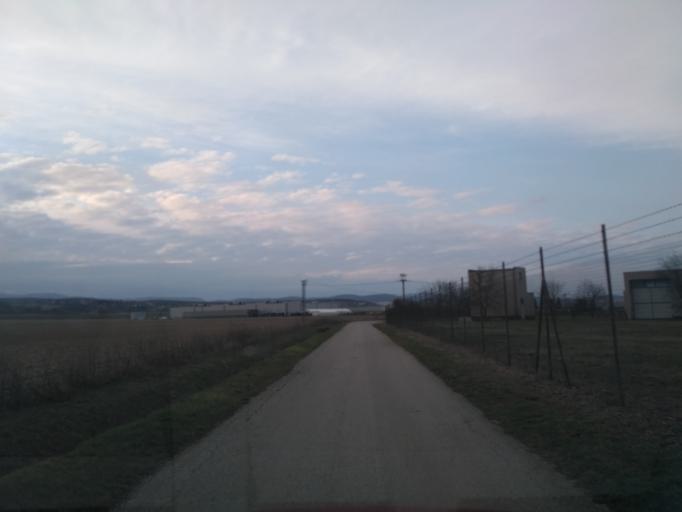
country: SK
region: Kosicky
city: Kosice
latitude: 48.6698
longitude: 21.2333
